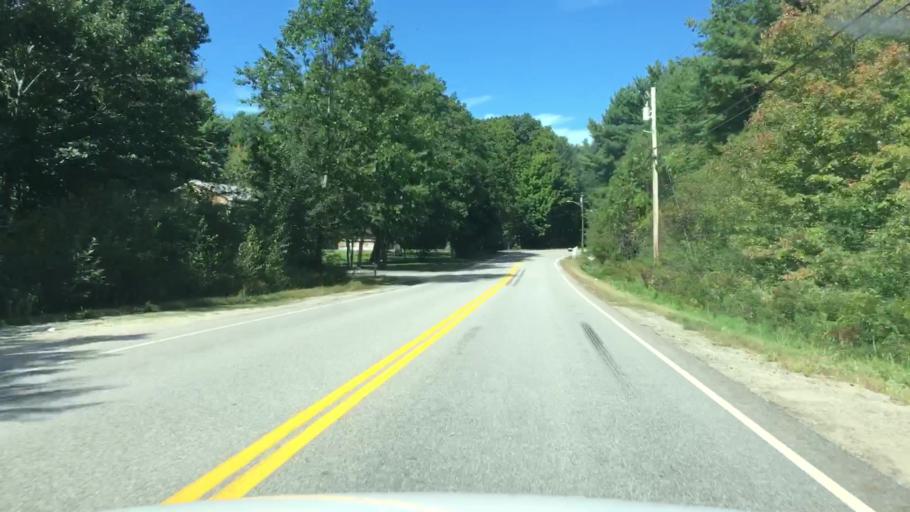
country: US
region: Maine
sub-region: Cumberland County
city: Westbrook
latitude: 43.6284
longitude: -70.4088
